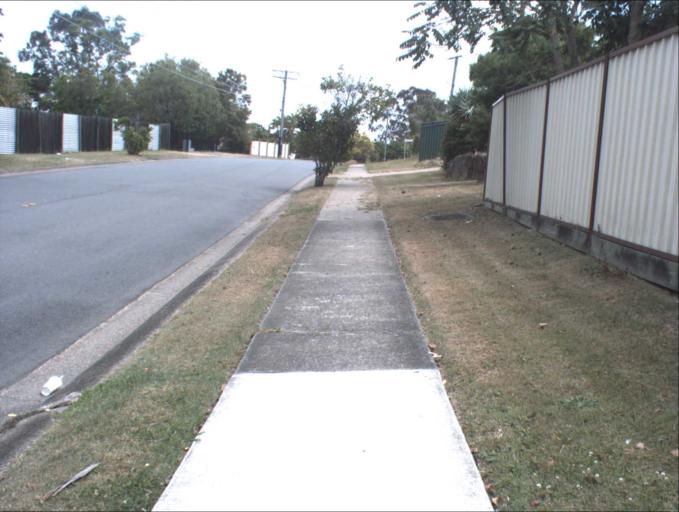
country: AU
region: Queensland
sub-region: Logan
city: Slacks Creek
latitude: -27.6574
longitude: 153.1805
